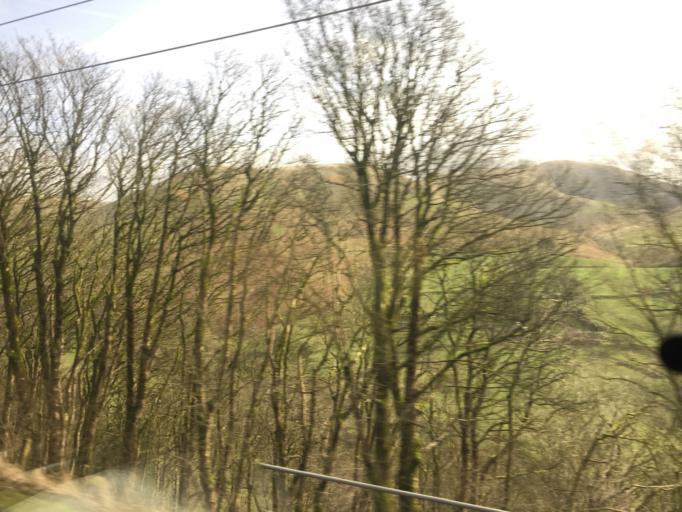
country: GB
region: England
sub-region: Cumbria
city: Sedbergh
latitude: 54.3741
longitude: -2.5824
